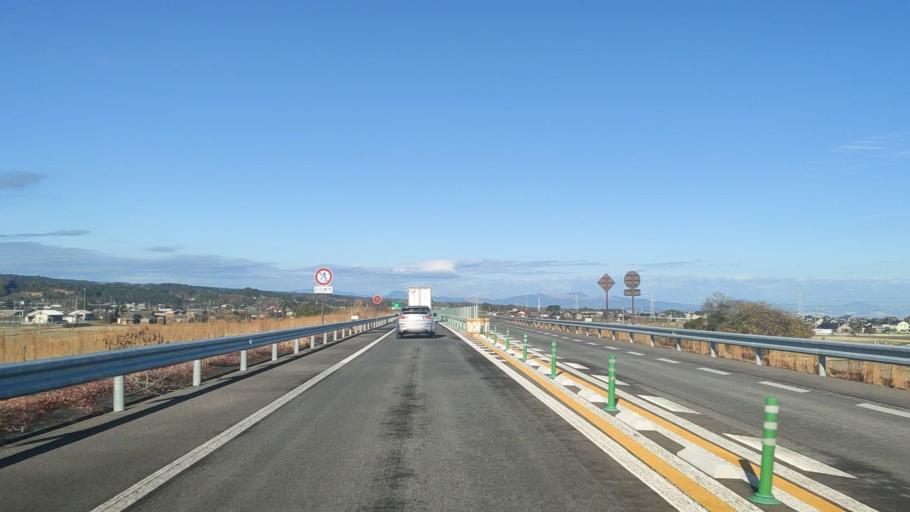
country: JP
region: Fukuoka
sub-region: Buzen-shi
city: Buzen
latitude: 33.5818
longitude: 131.1349
